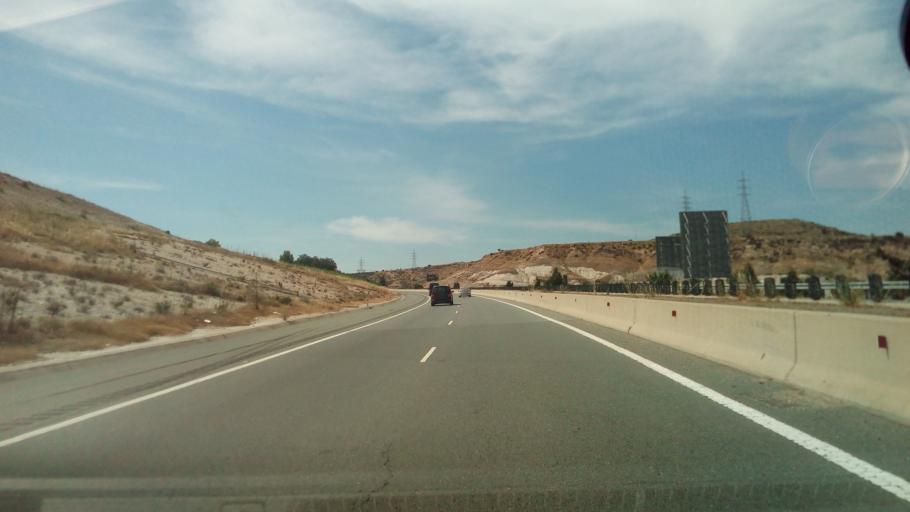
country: CY
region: Pafos
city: Mesogi
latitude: 34.7626
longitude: 32.4899
